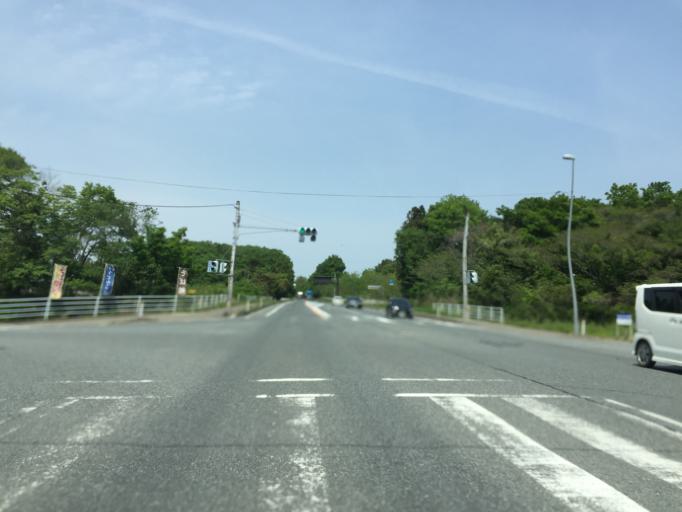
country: JP
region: Miyagi
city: Marumori
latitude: 37.8597
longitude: 140.9200
